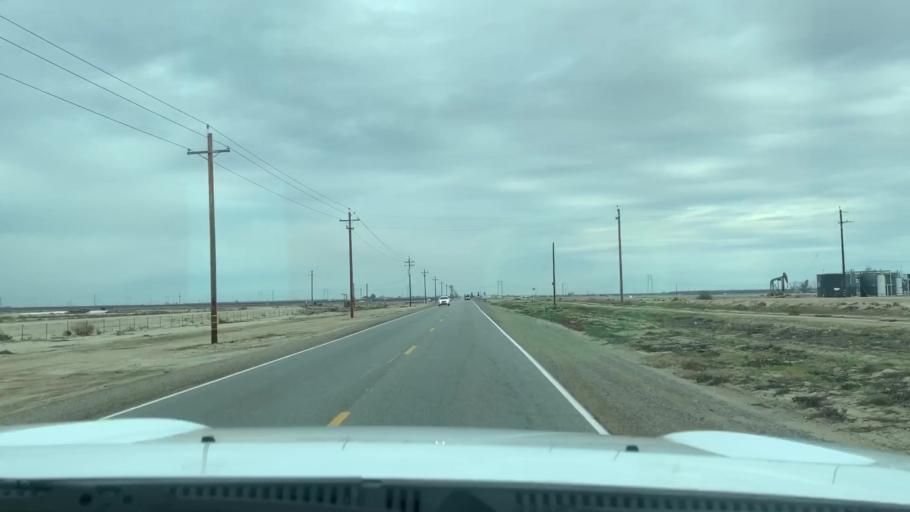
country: US
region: California
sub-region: Kern County
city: Rosedale
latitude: 35.3480
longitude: -119.2522
